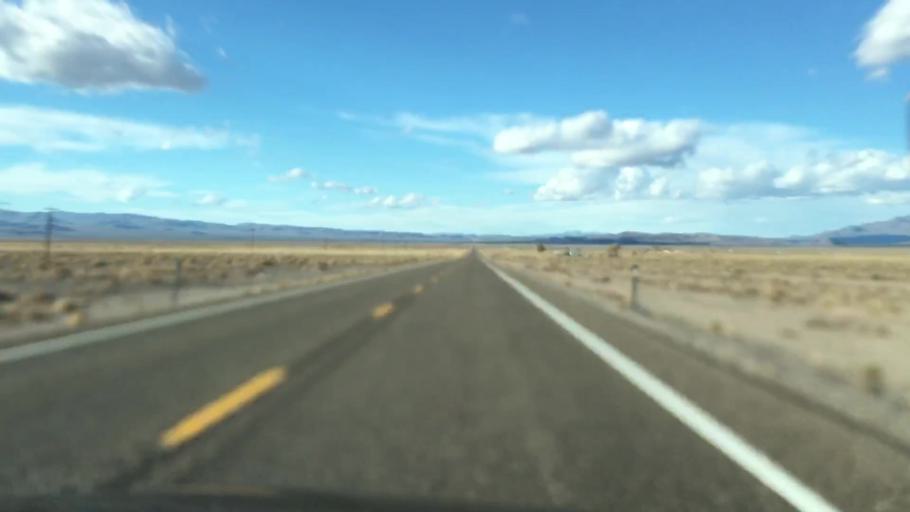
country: US
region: Nevada
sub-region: Nye County
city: Beatty
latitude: 37.2450
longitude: -116.9987
